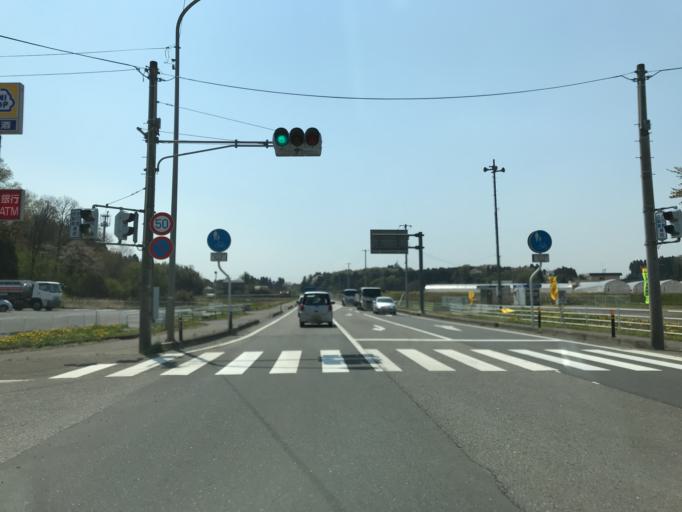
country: JP
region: Fukushima
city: Ishikawa
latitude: 37.1753
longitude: 140.3492
